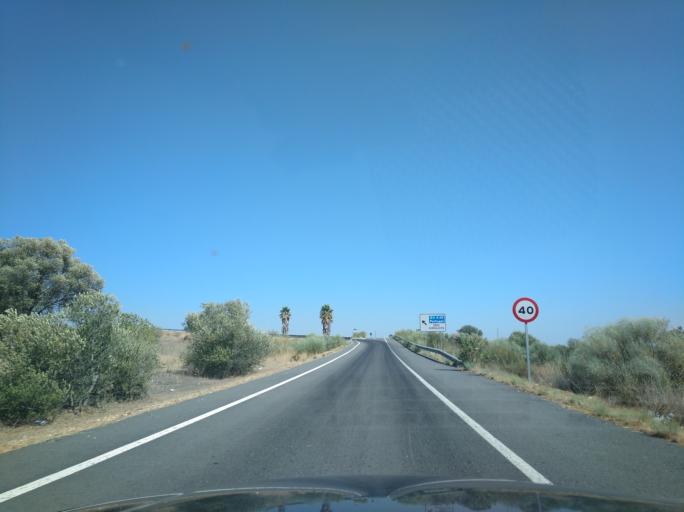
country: ES
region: Andalusia
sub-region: Provincia de Huelva
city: Aljaraque
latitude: 37.3344
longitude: -7.0243
